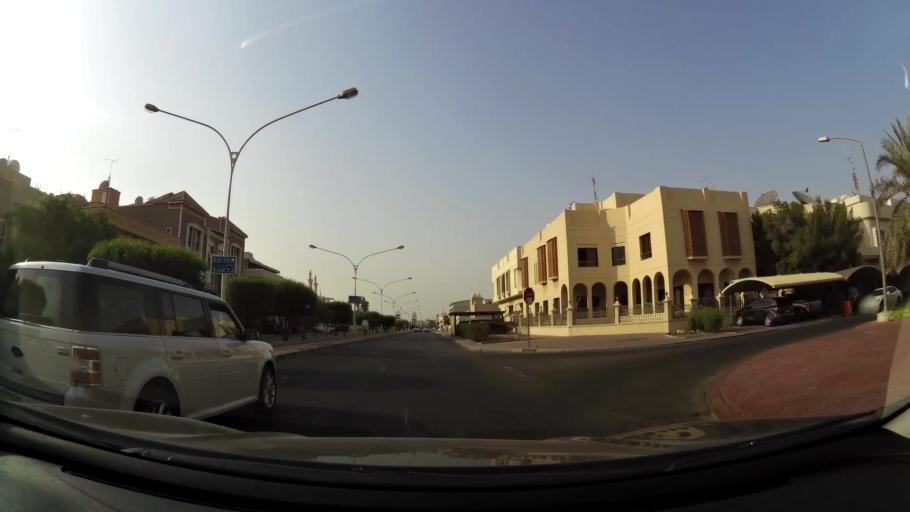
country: KW
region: Muhafazat Hawalli
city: Hawalli
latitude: 29.3111
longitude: 48.0074
